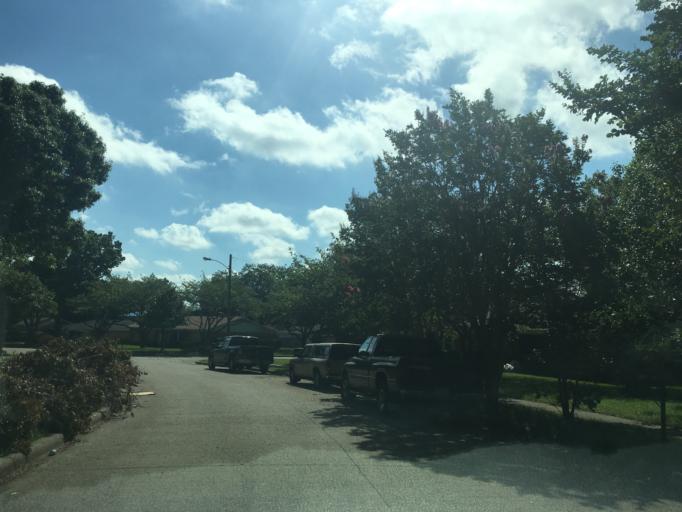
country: US
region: Texas
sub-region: Dallas County
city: Garland
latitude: 32.8464
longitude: -96.6635
